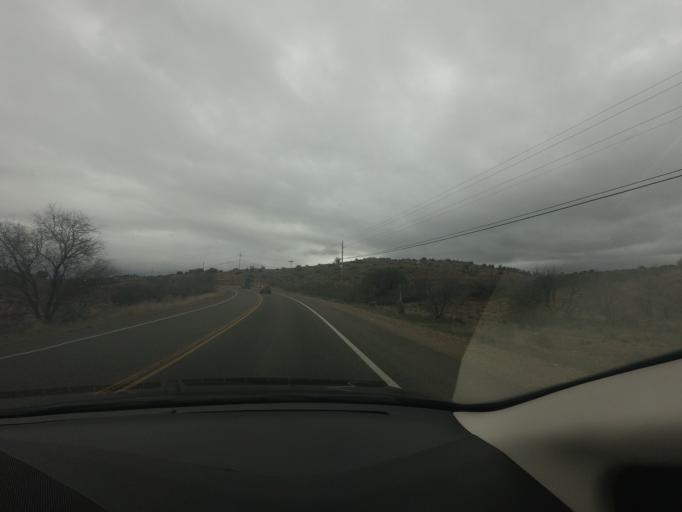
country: US
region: Arizona
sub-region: Yavapai County
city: Lake Montezuma
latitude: 34.6387
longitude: -111.8060
